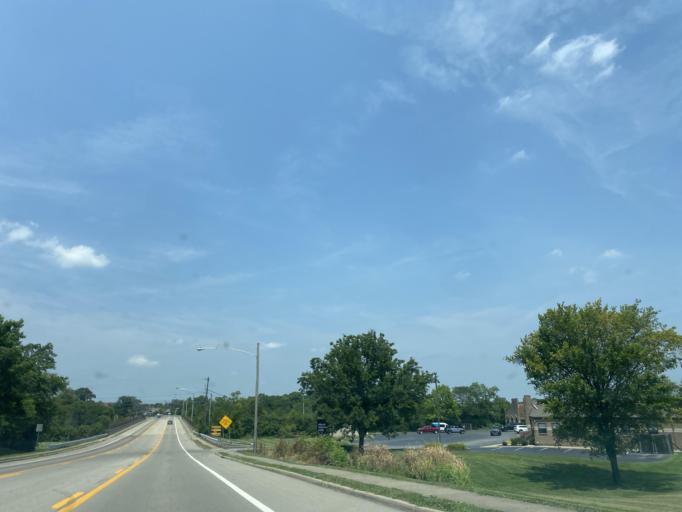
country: US
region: Kentucky
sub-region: Campbell County
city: Highland Heights
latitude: 39.0481
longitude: -84.4460
